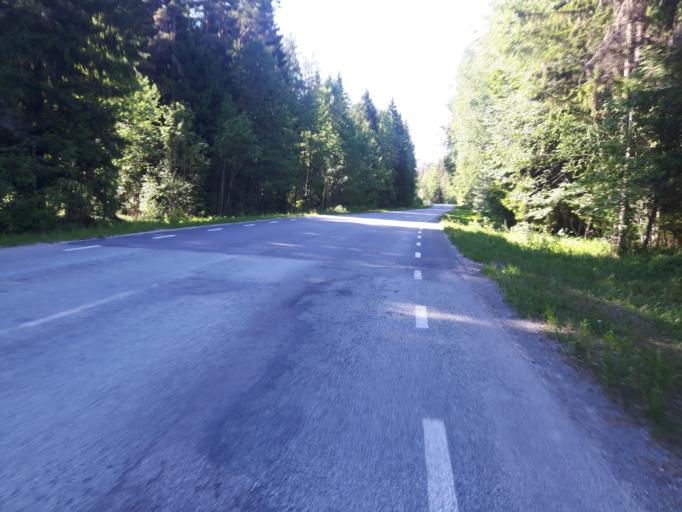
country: EE
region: Laeaene-Virumaa
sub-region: Kadrina vald
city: Kadrina
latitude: 59.5461
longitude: 26.0209
